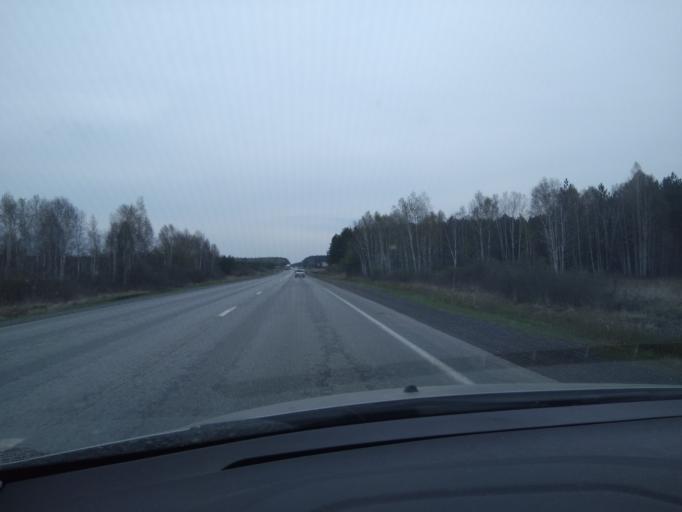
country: RU
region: Sverdlovsk
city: Baraba
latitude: 56.7858
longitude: 61.7518
